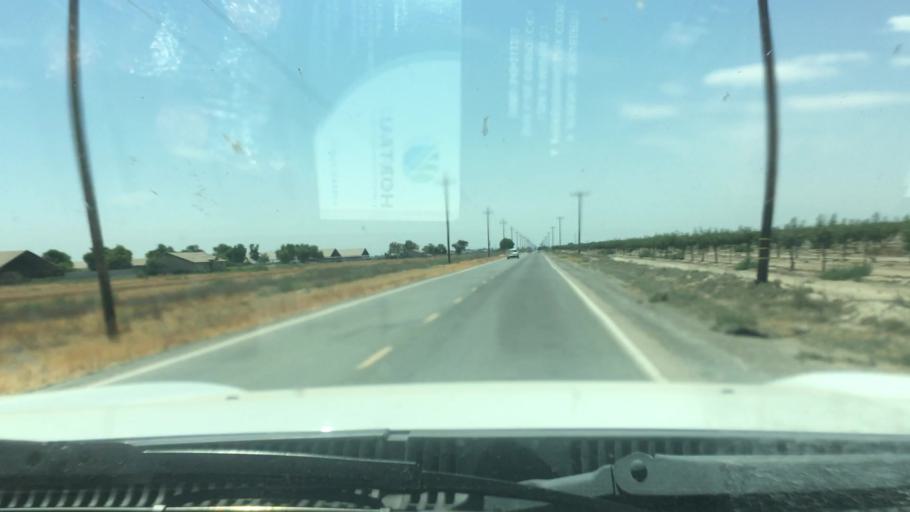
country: US
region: California
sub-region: Kings County
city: Corcoran
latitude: 36.0509
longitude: -119.4565
